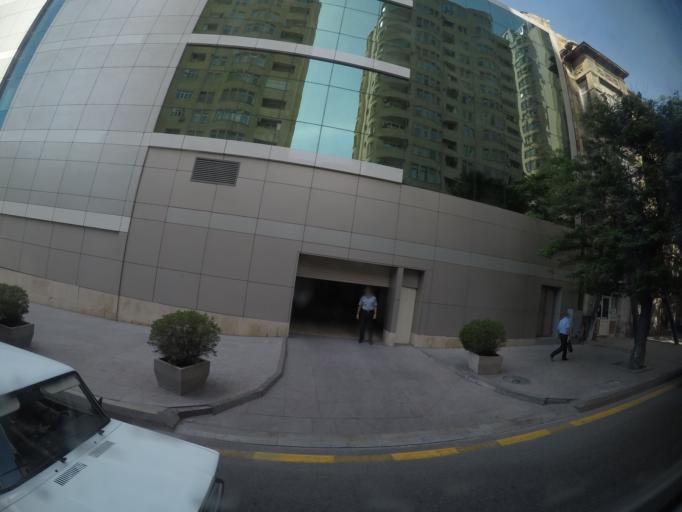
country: AZ
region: Baki
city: Badamdar
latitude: 40.3794
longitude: 49.8310
